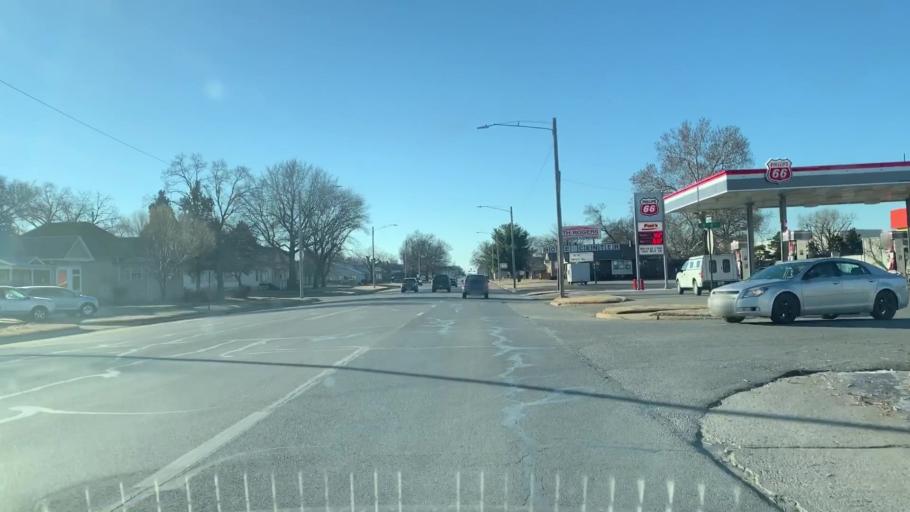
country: US
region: Kansas
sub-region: Crawford County
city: Pittsburg
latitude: 37.4239
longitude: -94.7050
